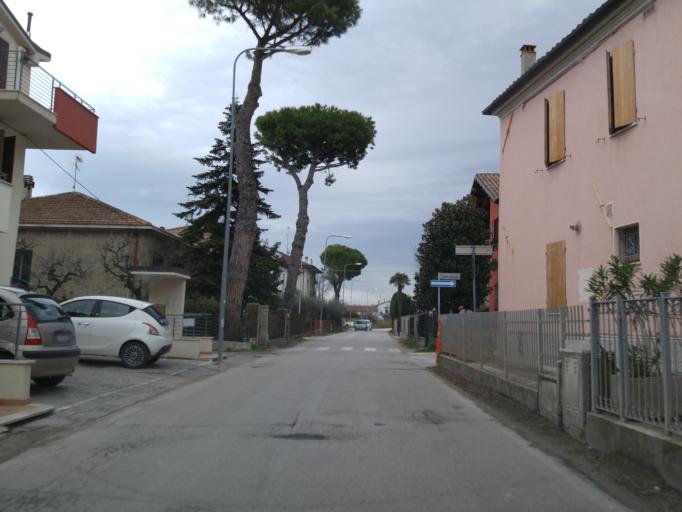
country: IT
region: The Marches
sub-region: Provincia di Pesaro e Urbino
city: Centinarola
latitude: 43.8402
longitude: 12.9976
